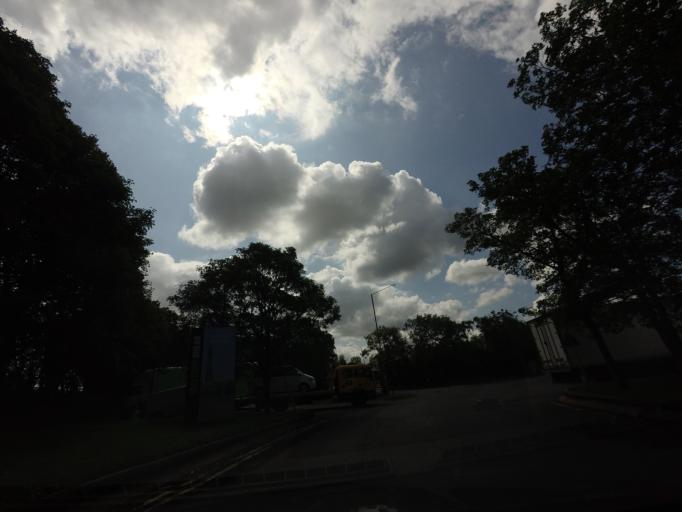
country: GB
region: England
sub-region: Lancashire
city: Coppull
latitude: 53.6310
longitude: -2.6888
